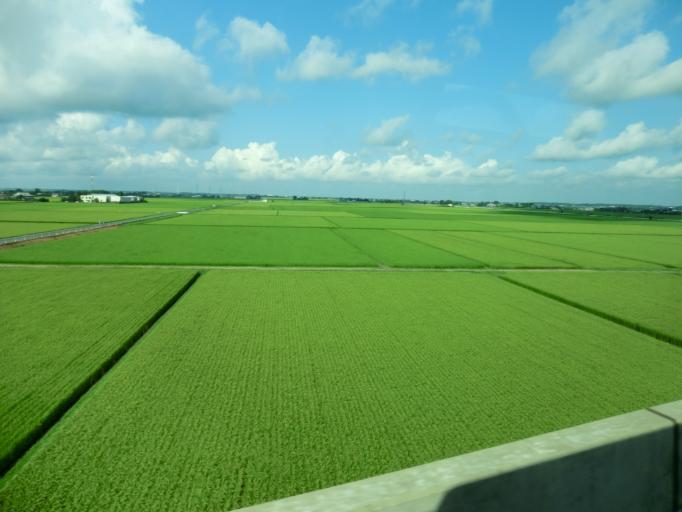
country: JP
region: Ibaraki
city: Inashiki
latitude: 35.9098
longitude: 140.3701
